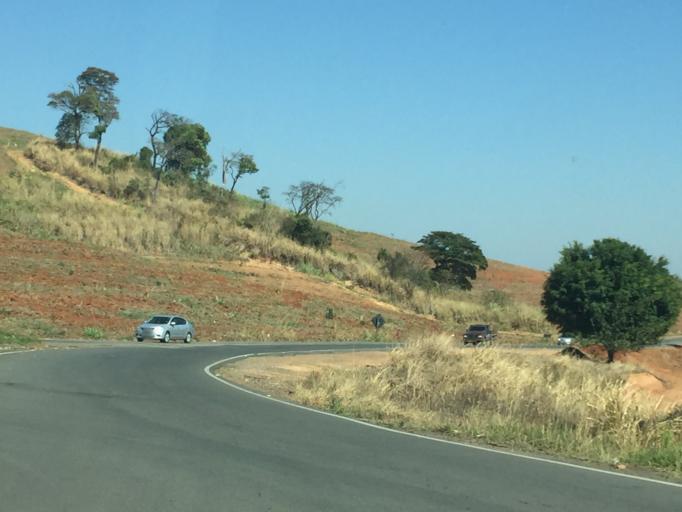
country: BR
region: Sao Paulo
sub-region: Itapira
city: Itapira
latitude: -22.4166
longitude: -46.7920
